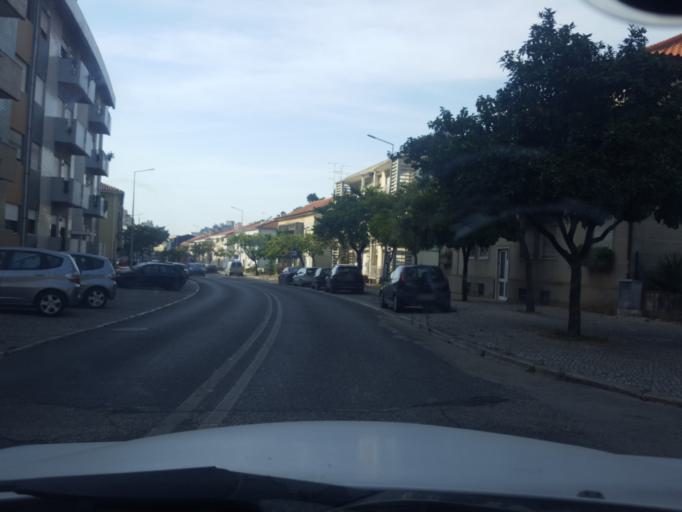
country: PT
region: Leiria
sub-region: Leiria
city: Leiria
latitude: 39.7366
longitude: -8.7994
